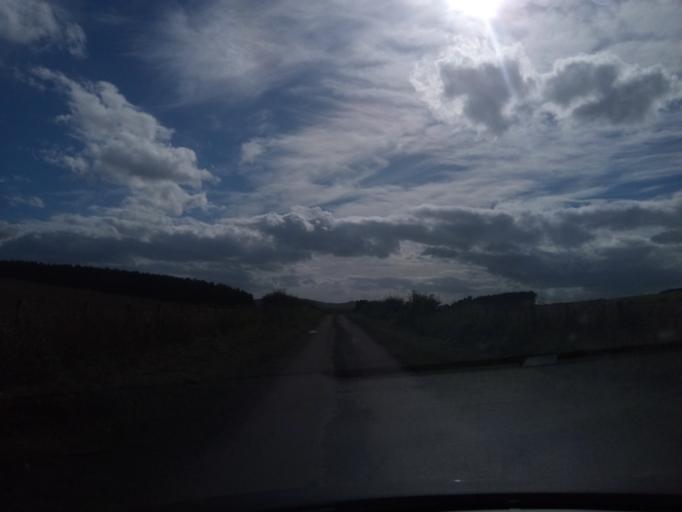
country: GB
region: England
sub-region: Northumberland
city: Kirknewton
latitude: 55.6056
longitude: -2.1834
